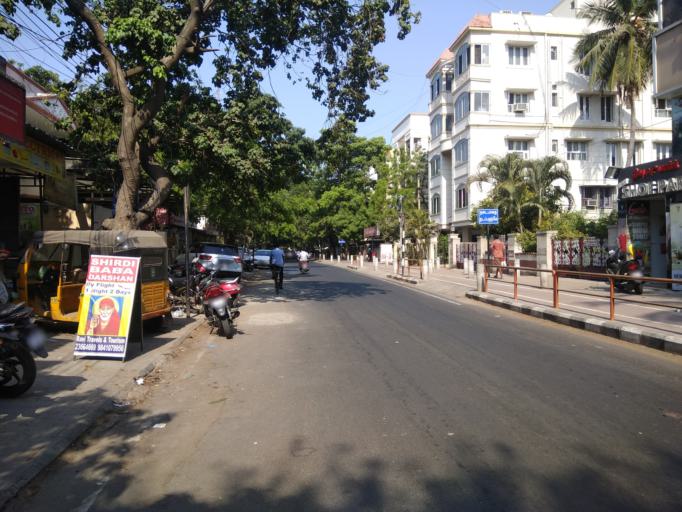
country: IN
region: Tamil Nadu
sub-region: Kancheepuram
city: Saint Thomas Mount
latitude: 13.0413
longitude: 80.1971
